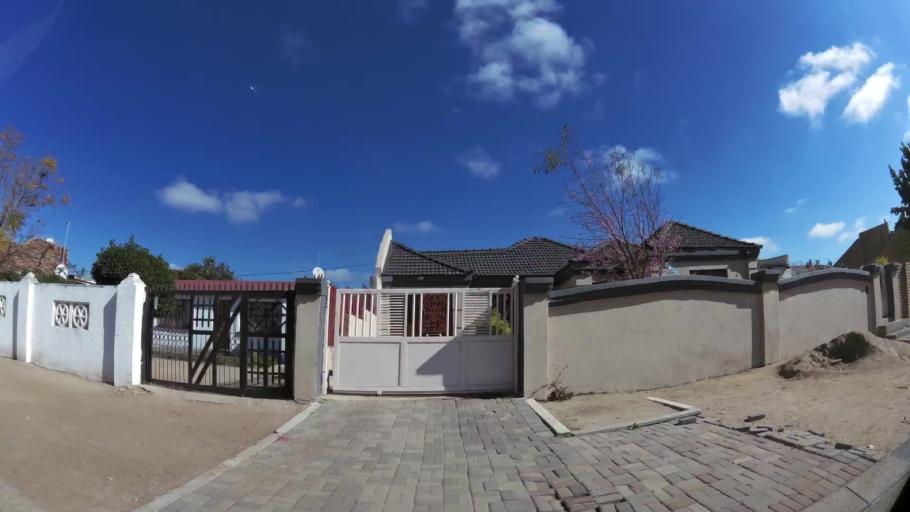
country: ZA
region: Limpopo
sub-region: Capricorn District Municipality
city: Polokwane
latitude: -23.8622
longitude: 29.3949
